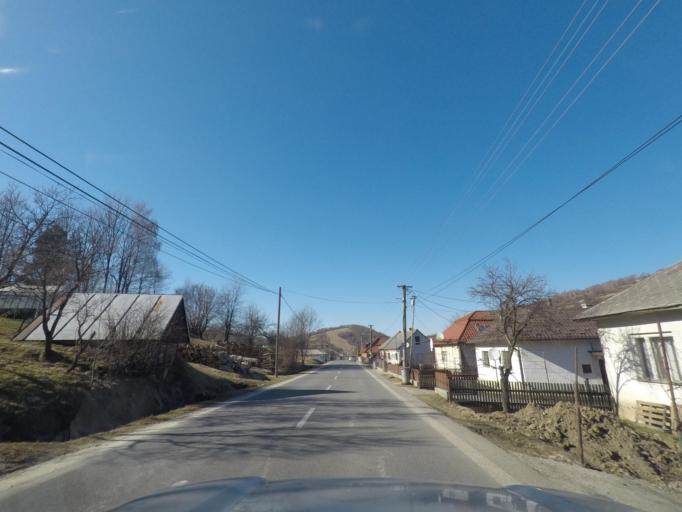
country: SK
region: Presovsky
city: Snina
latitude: 48.9605
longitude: 22.2535
